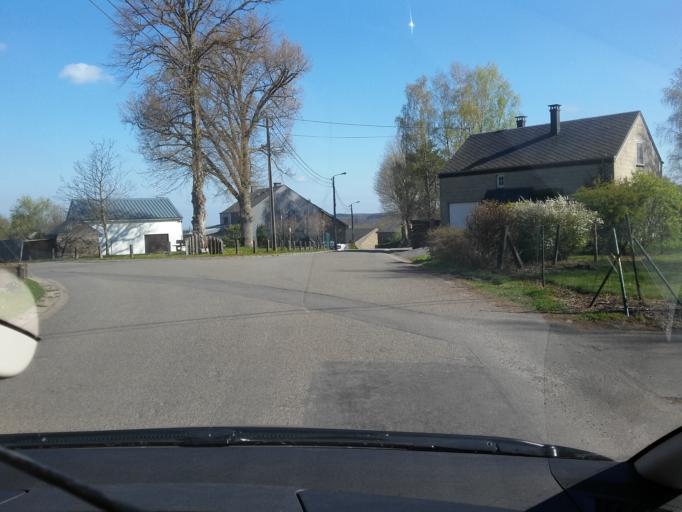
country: BE
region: Wallonia
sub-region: Province du Luxembourg
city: Libin
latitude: 50.0156
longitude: 5.2671
